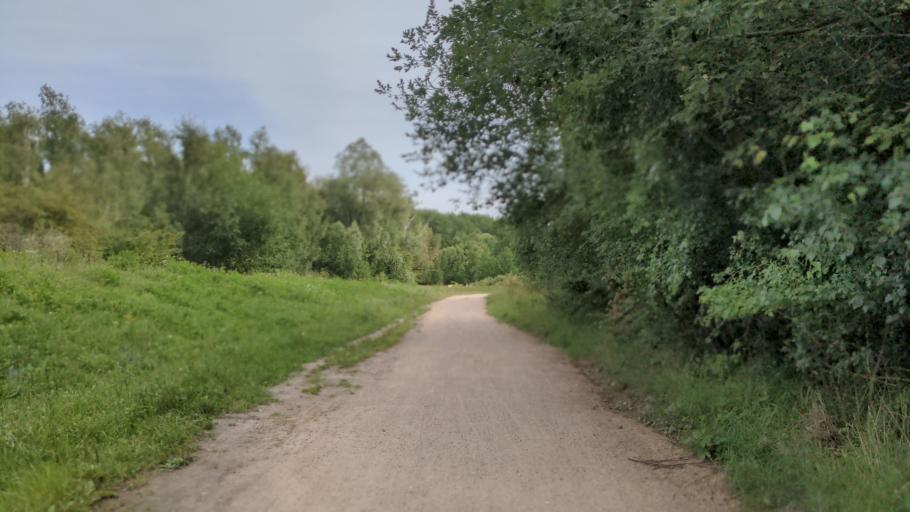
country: DE
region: Mecklenburg-Vorpommern
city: Ostseebad Boltenhagen
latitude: 53.9803
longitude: 11.2436
